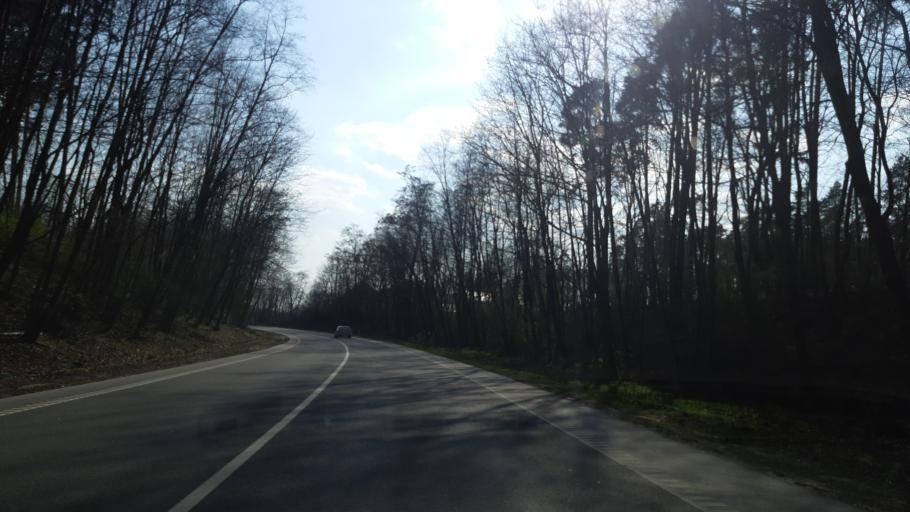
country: LT
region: Kauno apskritis
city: Dainava (Kaunas)
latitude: 54.8701
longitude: 23.9889
